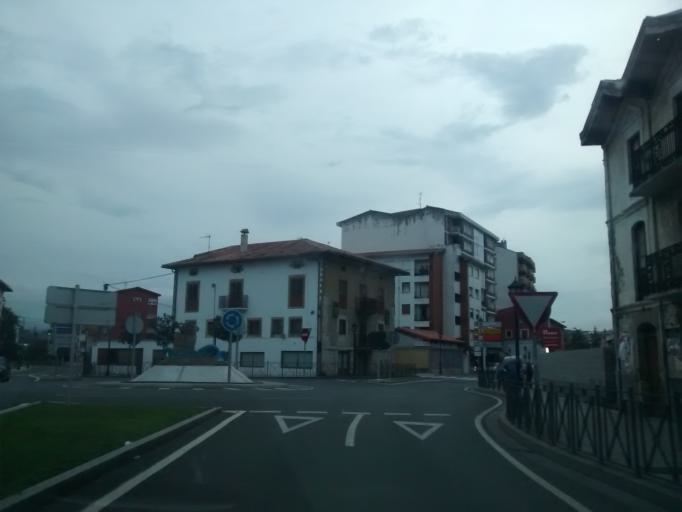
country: ES
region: Cantabria
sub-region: Provincia de Cantabria
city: Colindres
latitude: 43.3955
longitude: -3.4490
